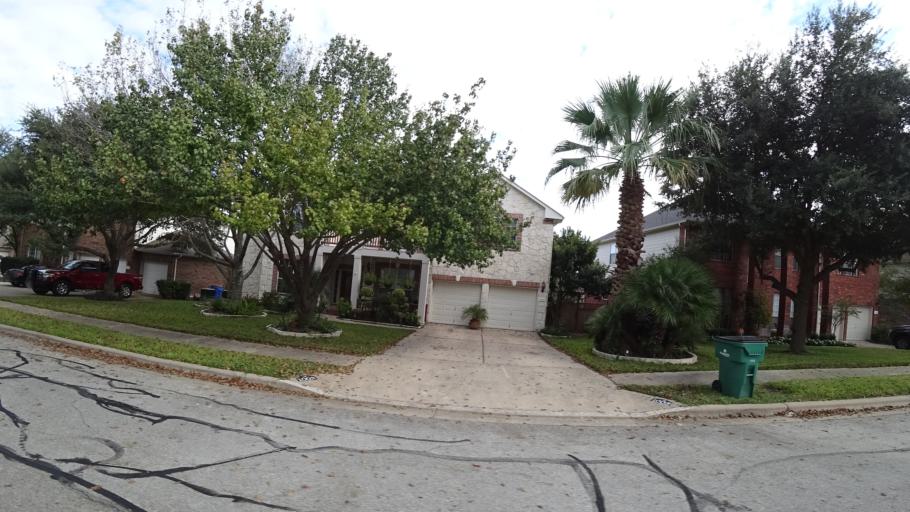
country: US
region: Texas
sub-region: Travis County
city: Pflugerville
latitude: 30.4304
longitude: -97.6279
